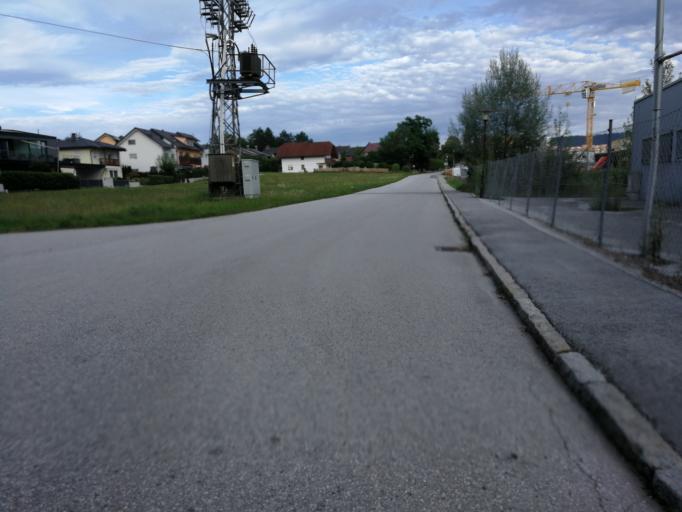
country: AT
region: Salzburg
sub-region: Politischer Bezirk Salzburg-Umgebung
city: Elixhausen
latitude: 47.8639
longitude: 13.0587
